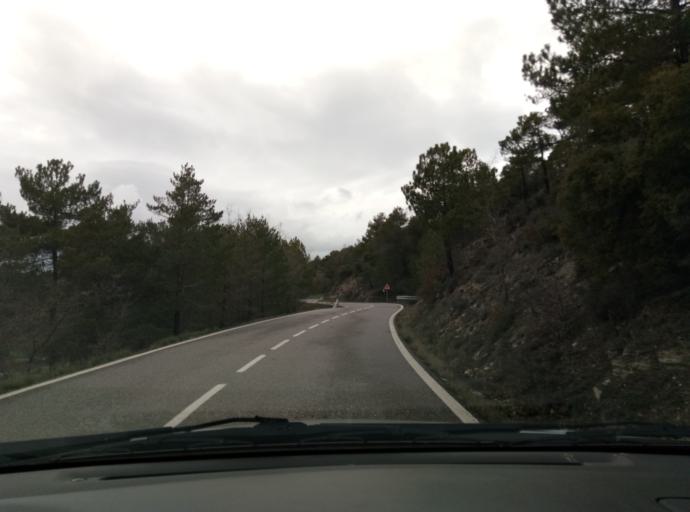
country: ES
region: Catalonia
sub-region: Provincia de Tarragona
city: Conesa
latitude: 41.5442
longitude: 1.3262
